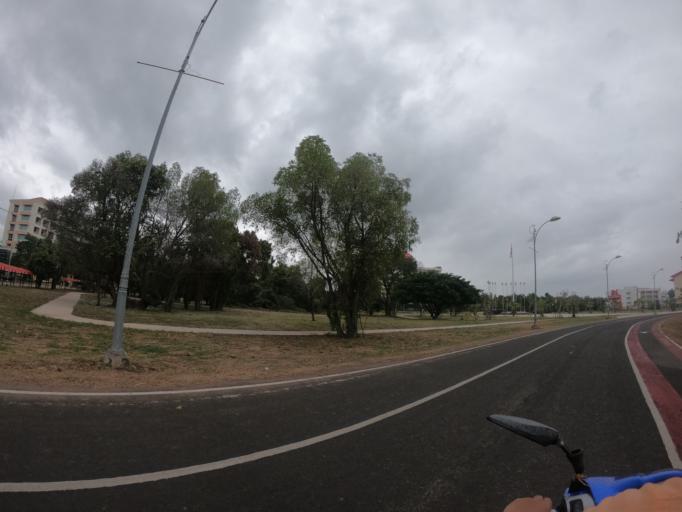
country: TH
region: Roi Et
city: Selaphum
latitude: 16.1418
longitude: 103.8804
